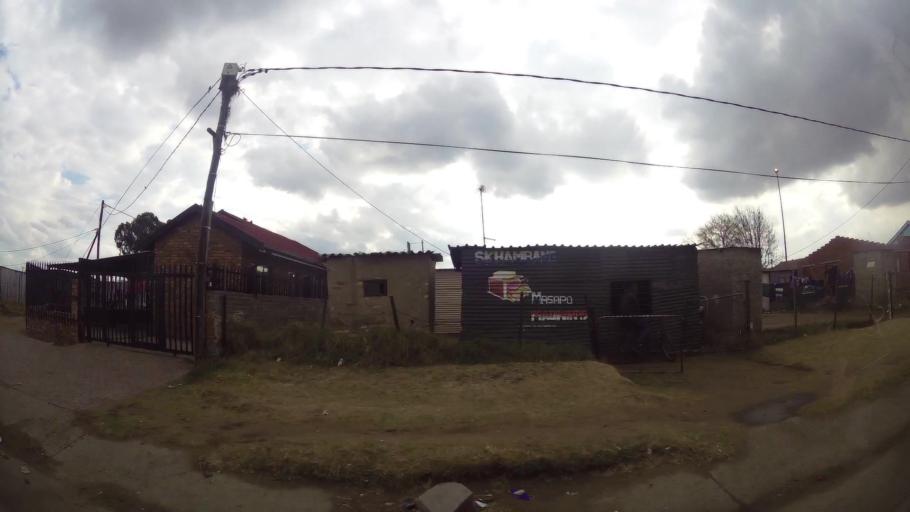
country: ZA
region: Orange Free State
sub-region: Fezile Dabi District Municipality
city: Sasolburg
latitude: -26.8521
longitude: 27.8613
